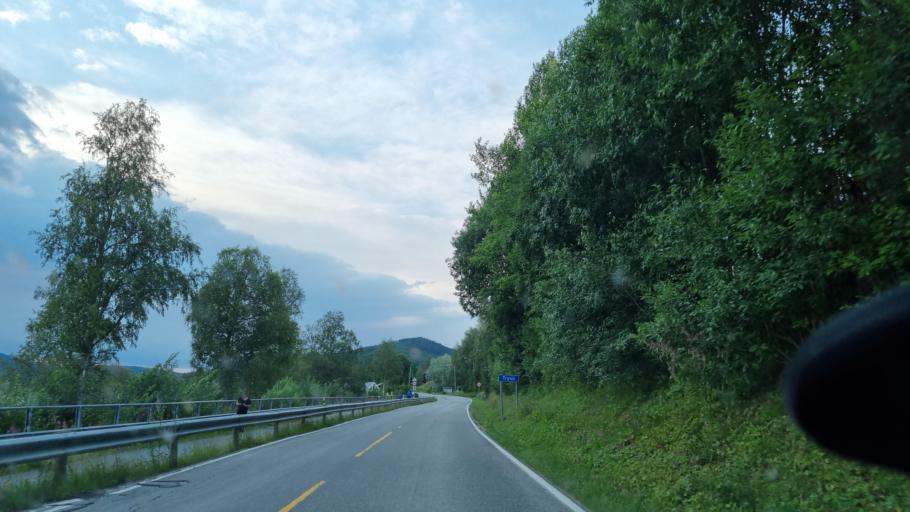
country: NO
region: Hedmark
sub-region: Trysil
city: Innbygda
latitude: 61.3072
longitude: 12.2729
